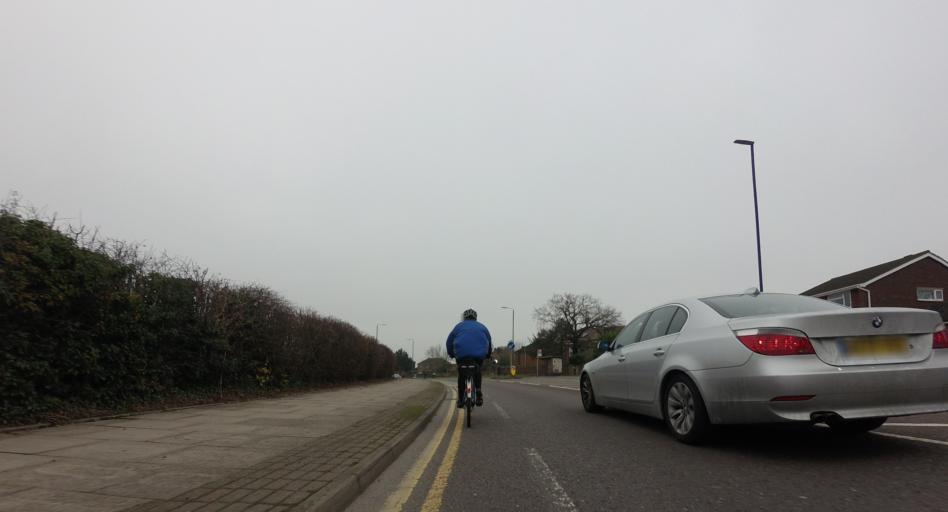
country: GB
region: England
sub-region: Greater London
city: Bexley
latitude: 51.4518
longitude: 0.1524
